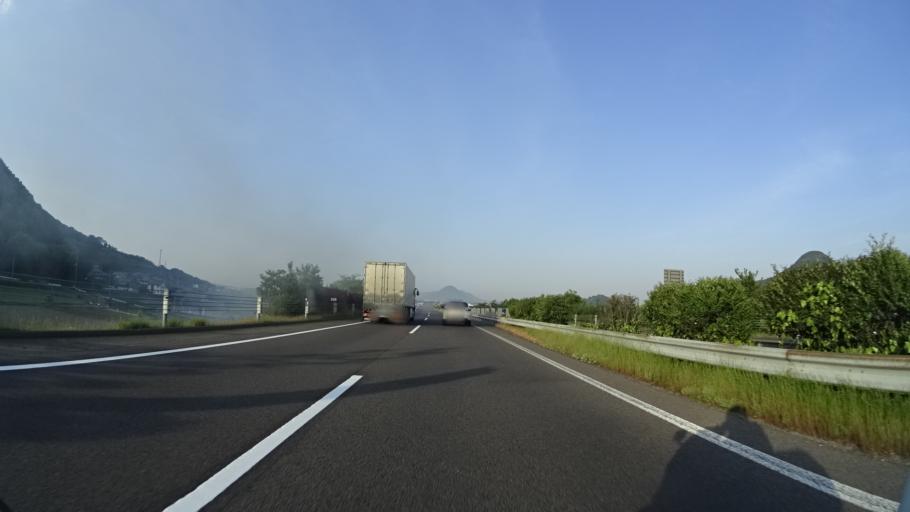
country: JP
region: Kagawa
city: Tadotsu
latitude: 34.2289
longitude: 133.7422
